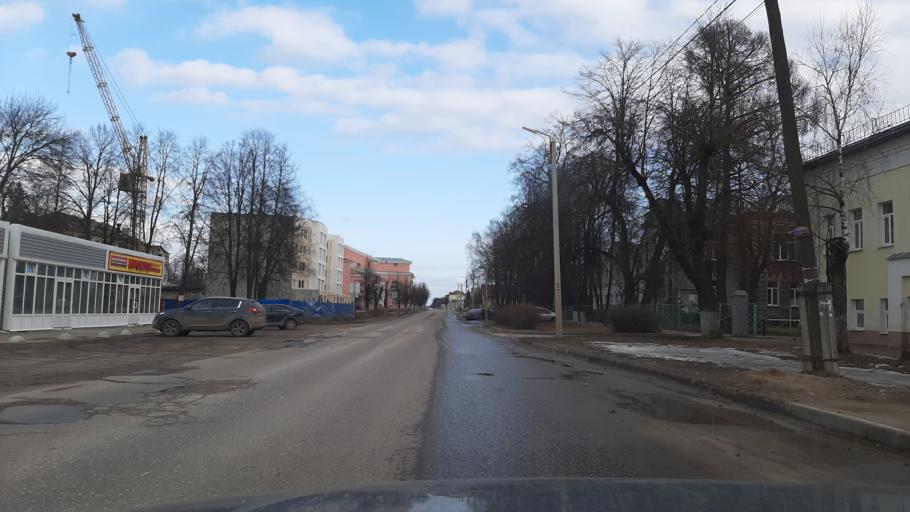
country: RU
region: Ivanovo
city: Teykovo
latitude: 56.8545
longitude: 40.5296
